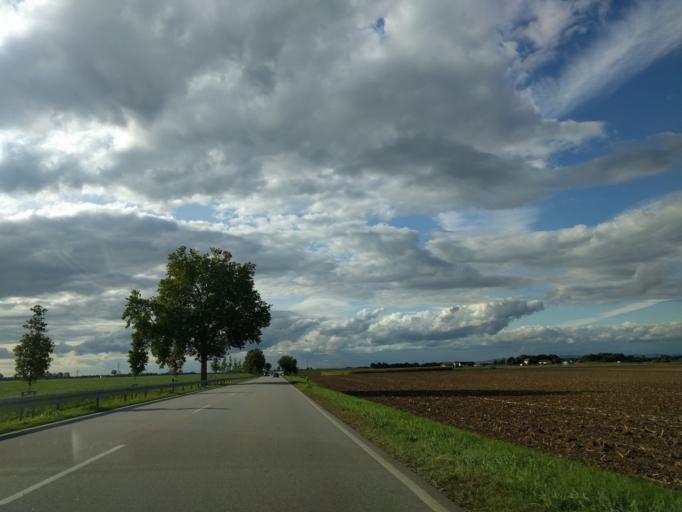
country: DE
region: Bavaria
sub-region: Lower Bavaria
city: Stephansposching
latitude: 48.8029
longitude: 12.7970
